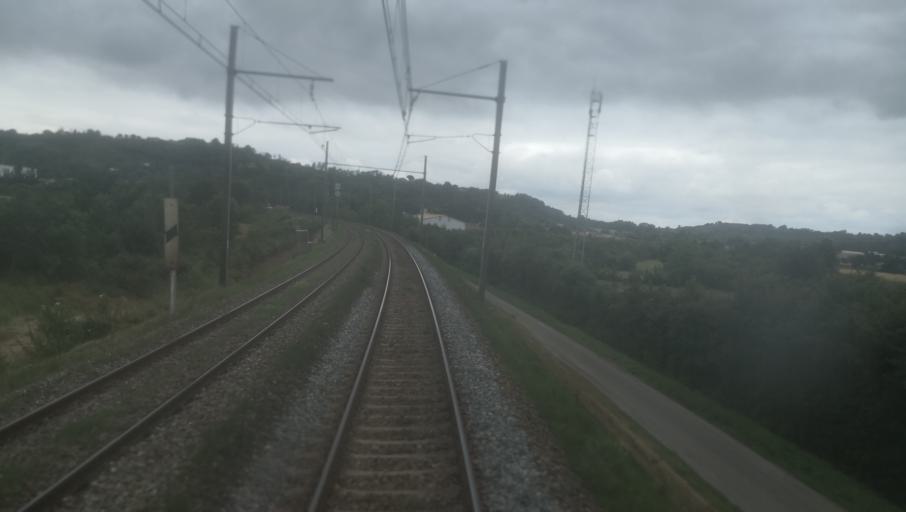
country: FR
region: Midi-Pyrenees
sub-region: Departement du Tarn-et-Garonne
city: Moissac
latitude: 44.1002
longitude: 1.1058
